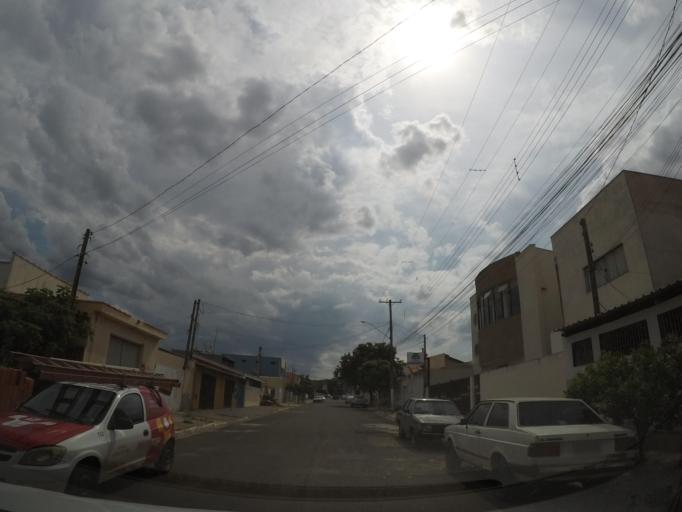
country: BR
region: Sao Paulo
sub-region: Sumare
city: Sumare
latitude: -22.8135
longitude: -47.2384
